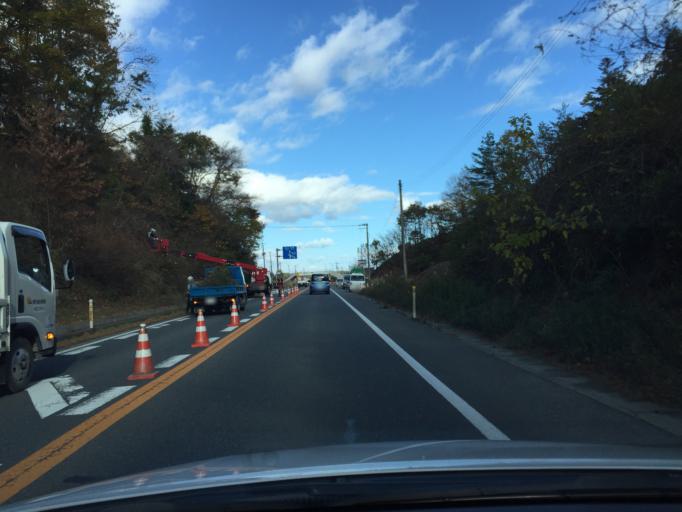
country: JP
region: Fukushima
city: Namie
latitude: 37.5487
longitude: 141.0062
